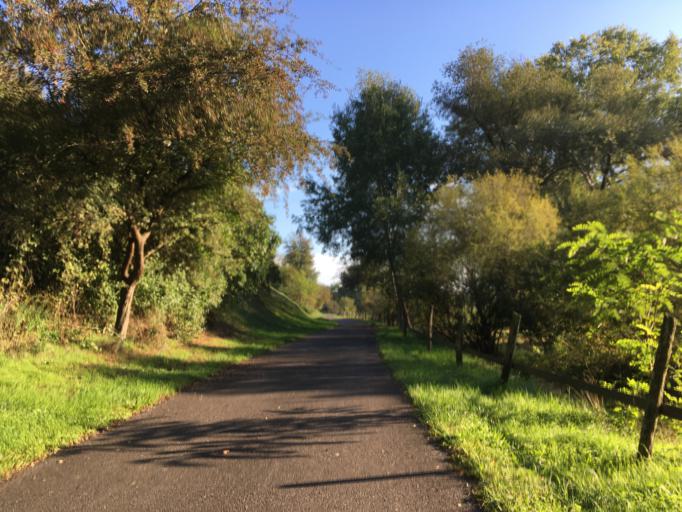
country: DE
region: Brandenburg
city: Lebus
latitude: 52.4361
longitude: 14.5454
